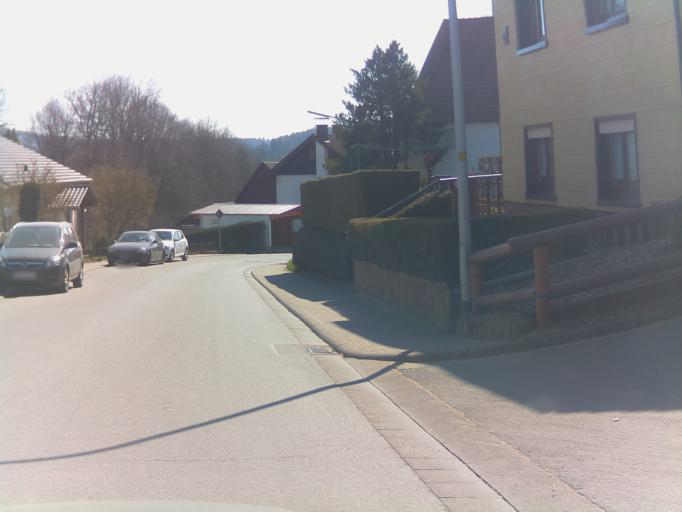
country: DE
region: Hesse
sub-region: Regierungsbezirk Darmstadt
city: Wald-Michelbach
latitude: 49.5893
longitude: 8.8151
